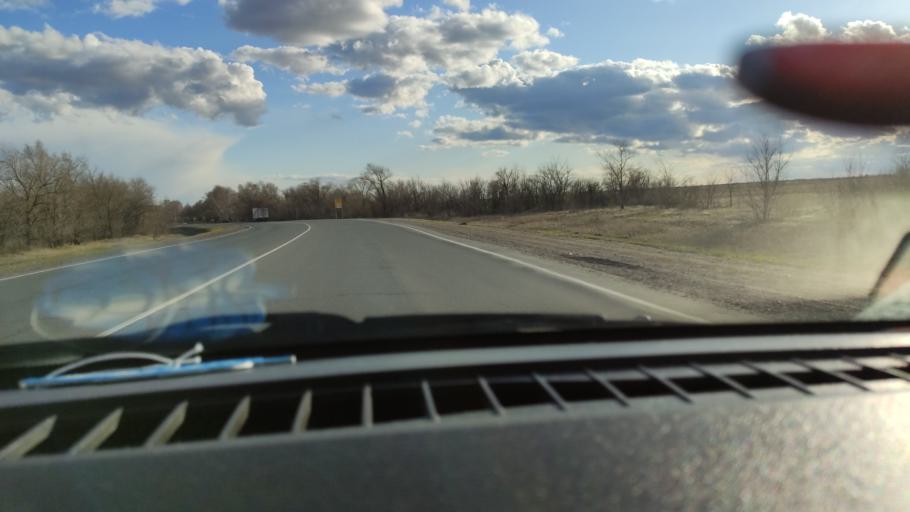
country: RU
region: Saratov
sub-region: Saratovskiy Rayon
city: Saratov
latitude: 51.7043
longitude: 46.0131
